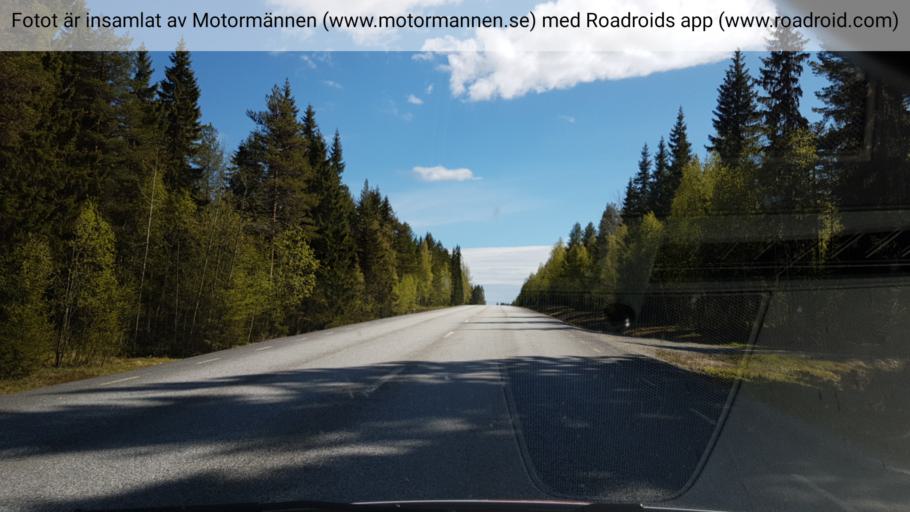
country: SE
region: Vaesterbotten
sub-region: Vannas Kommun
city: Vannasby
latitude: 64.0902
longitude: 19.9732
